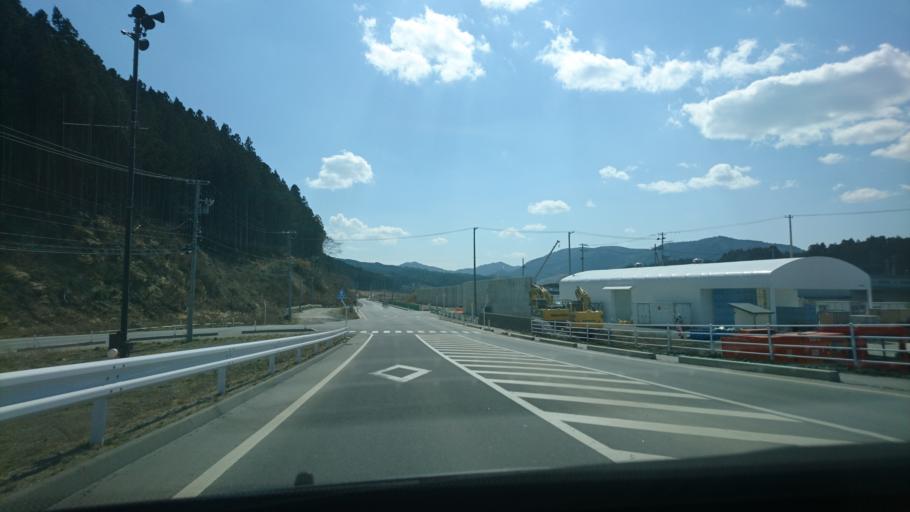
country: JP
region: Miyagi
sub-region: Oshika Gun
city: Onagawa Cho
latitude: 38.6418
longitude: 141.4623
